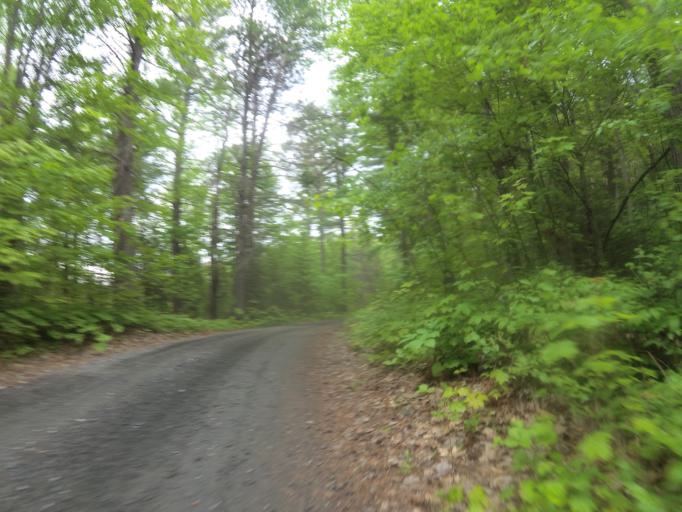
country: CA
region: Ontario
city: Renfrew
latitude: 45.1030
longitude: -76.8286
